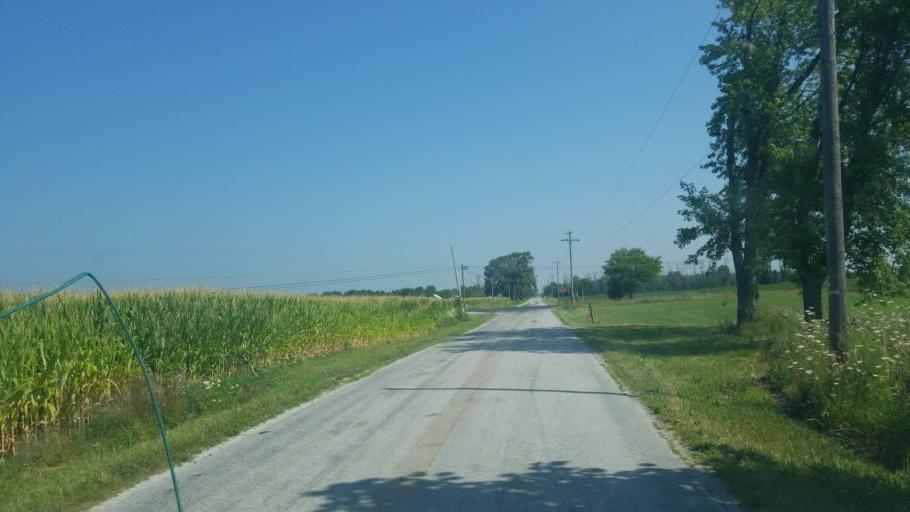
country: US
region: Ohio
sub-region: Hardin County
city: Kenton
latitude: 40.6703
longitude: -83.5380
